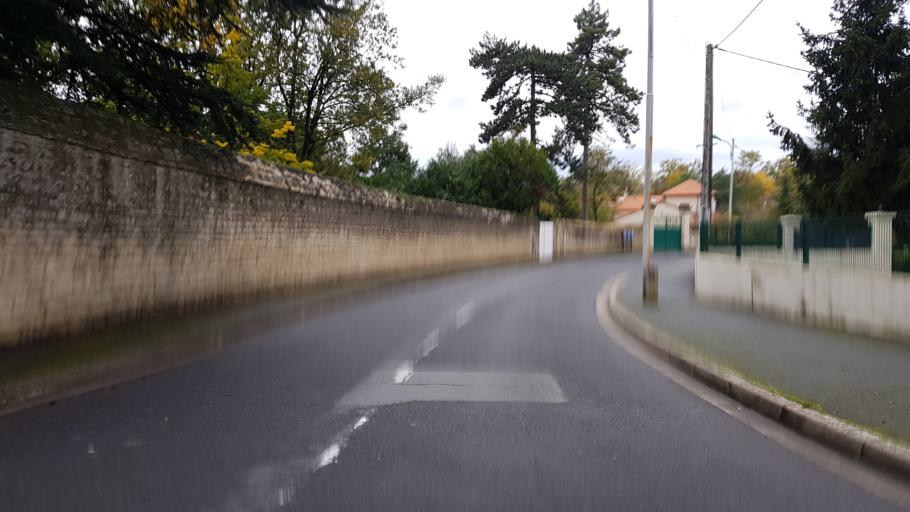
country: FR
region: Poitou-Charentes
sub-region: Departement de la Vienne
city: Chasseneuil-du-Poitou
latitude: 46.6536
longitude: 0.3794
